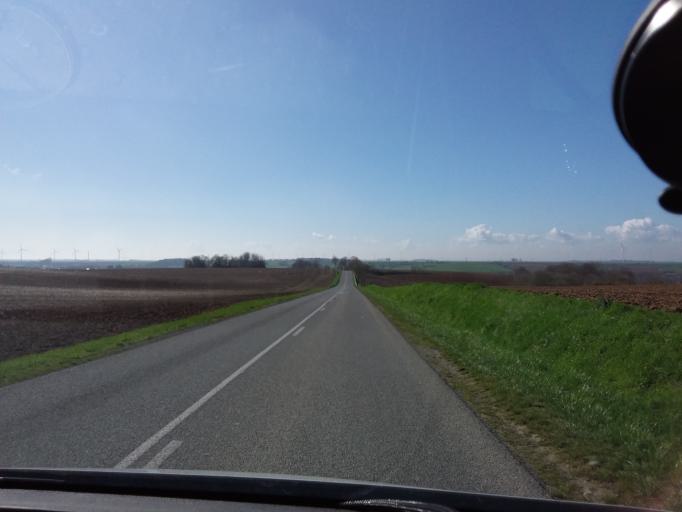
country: FR
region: Picardie
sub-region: Departement de l'Aisne
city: Montcornet
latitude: 49.7121
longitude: 4.0177
